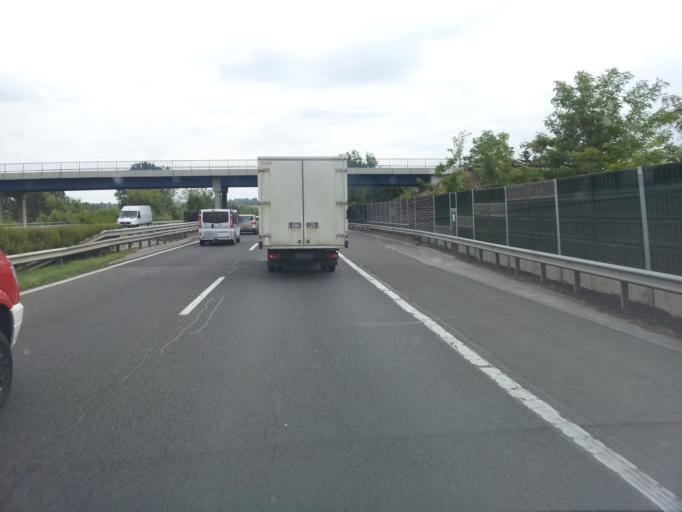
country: HU
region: Pest
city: Bag
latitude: 47.6379
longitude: 19.4806
